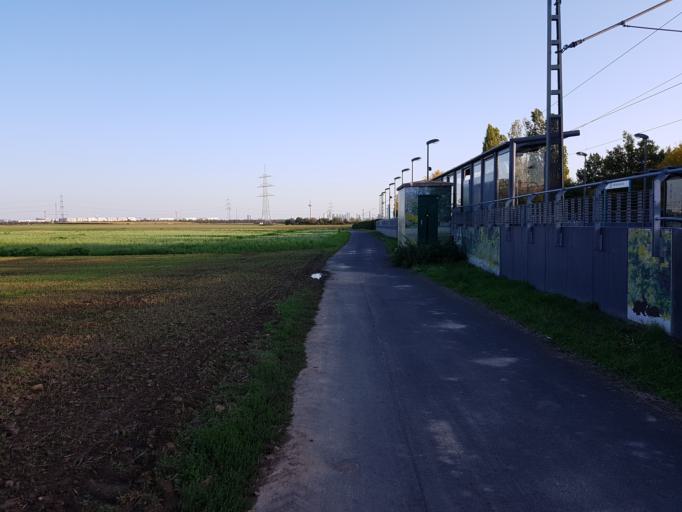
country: DE
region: Hesse
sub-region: Regierungsbezirk Darmstadt
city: Oberursel
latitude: 50.1859
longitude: 8.6027
